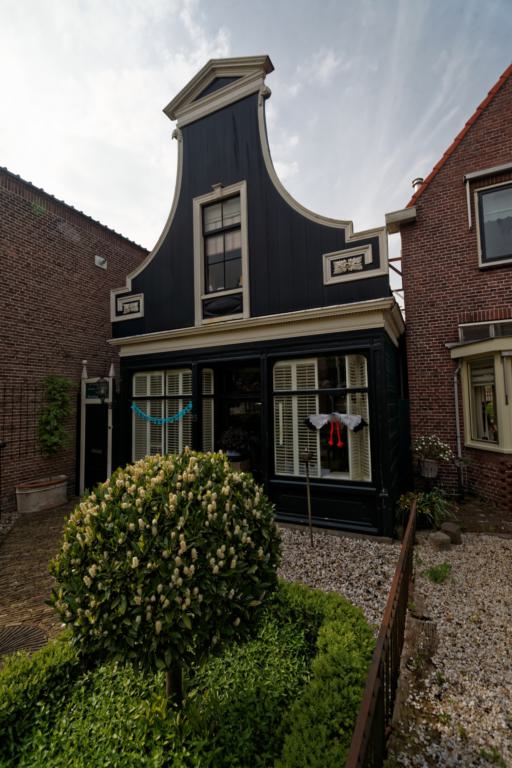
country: NL
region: North Holland
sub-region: Gemeente Zaanstad
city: Zaanstad
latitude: 52.4735
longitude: 4.8132
